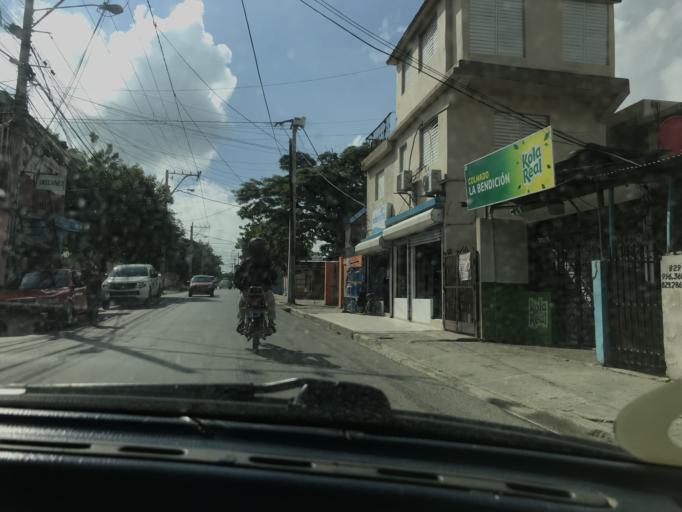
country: DO
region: Santiago
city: Santiago de los Caballeros
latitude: 19.4549
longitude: -70.7191
